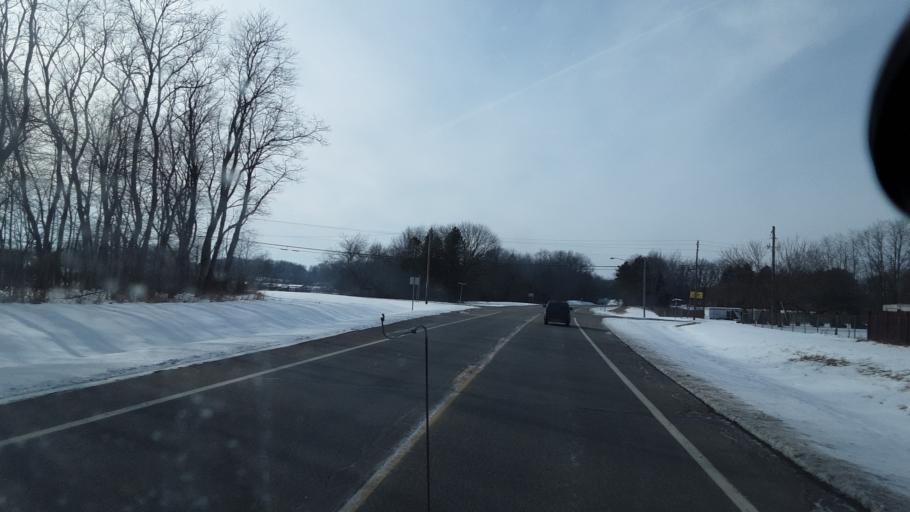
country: US
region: Ohio
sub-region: Stark County
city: Hartville
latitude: 41.0302
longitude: -81.2680
